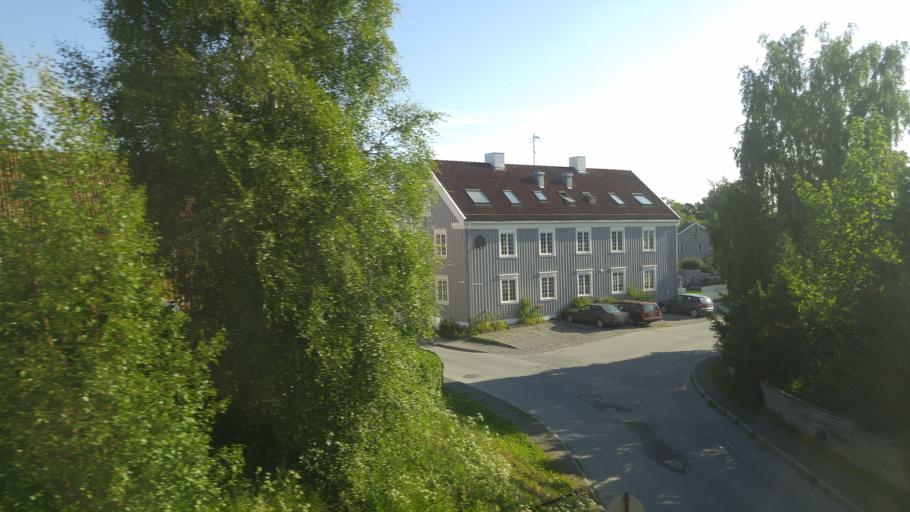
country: NO
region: Sor-Trondelag
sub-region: Trondheim
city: Trondheim
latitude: 63.4357
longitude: 10.4910
